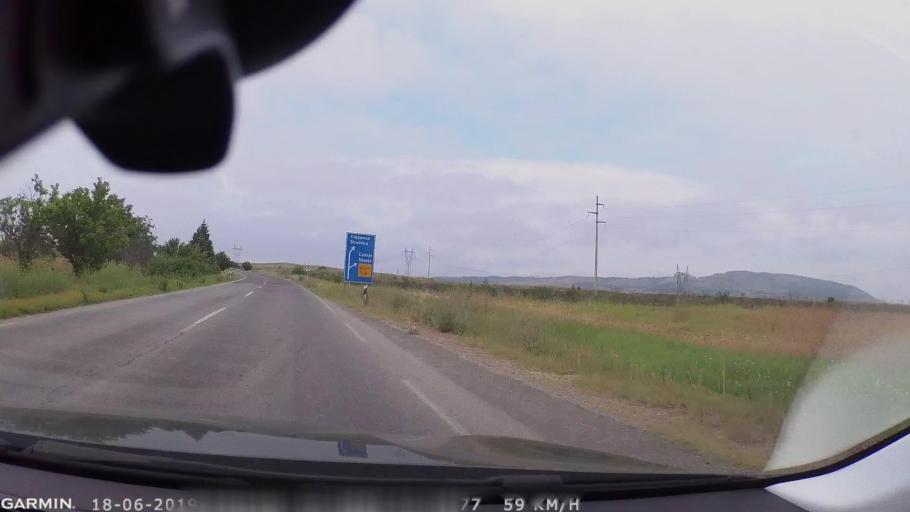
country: MK
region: Stip
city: Shtip
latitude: 41.7677
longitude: 22.1654
